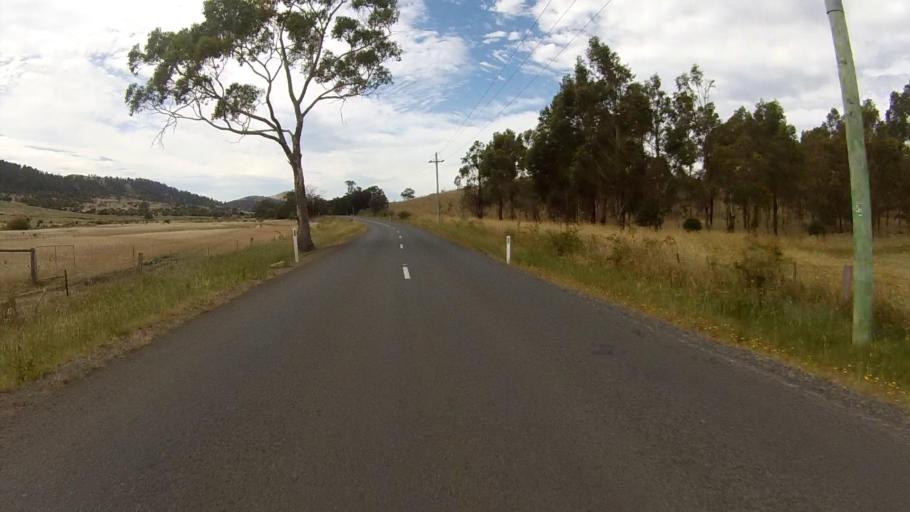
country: AU
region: Tasmania
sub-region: Clarence
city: Cambridge
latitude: -42.7168
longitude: 147.3853
